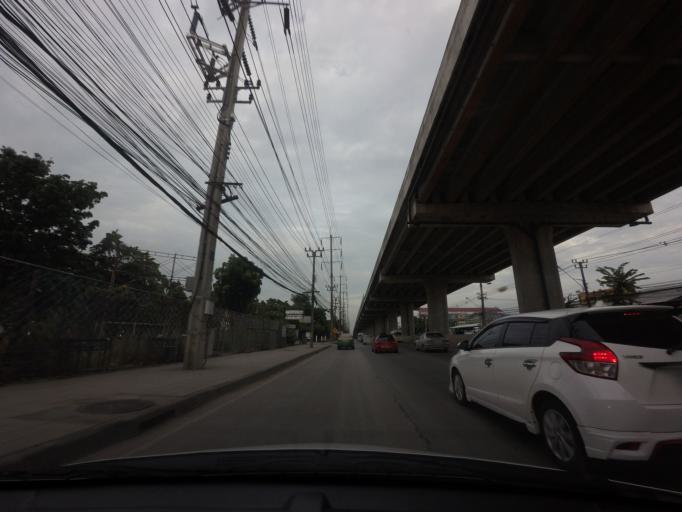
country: TH
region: Bangkok
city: Min Buri
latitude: 13.8159
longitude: 100.7471
